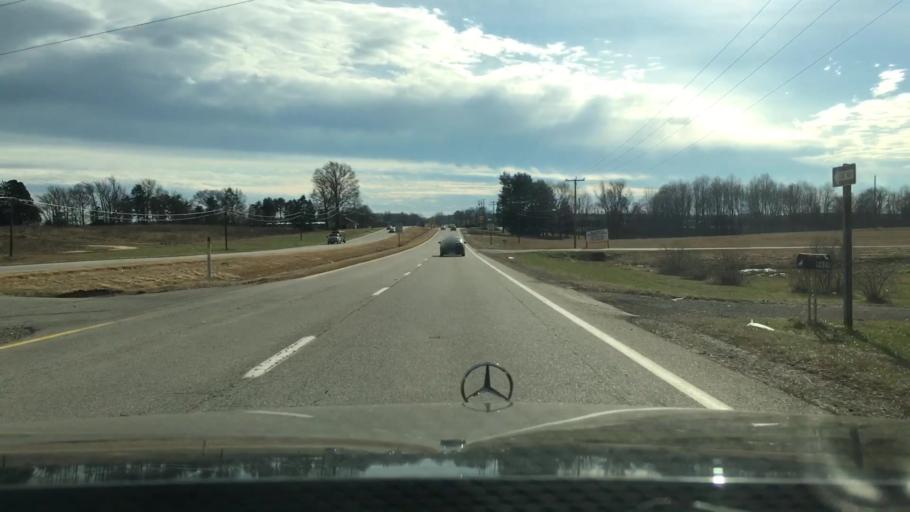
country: US
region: Virginia
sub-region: Pittsylvania County
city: Mount Hermon
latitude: 36.7384
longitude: -79.3800
